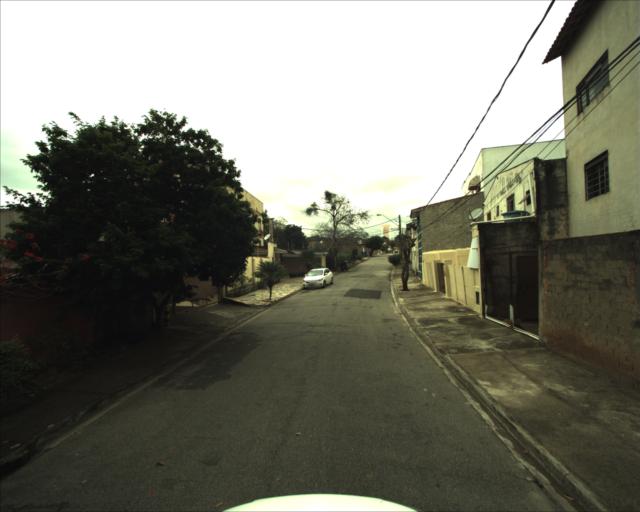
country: BR
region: Sao Paulo
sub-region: Sorocaba
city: Sorocaba
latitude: -23.5003
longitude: -47.4885
